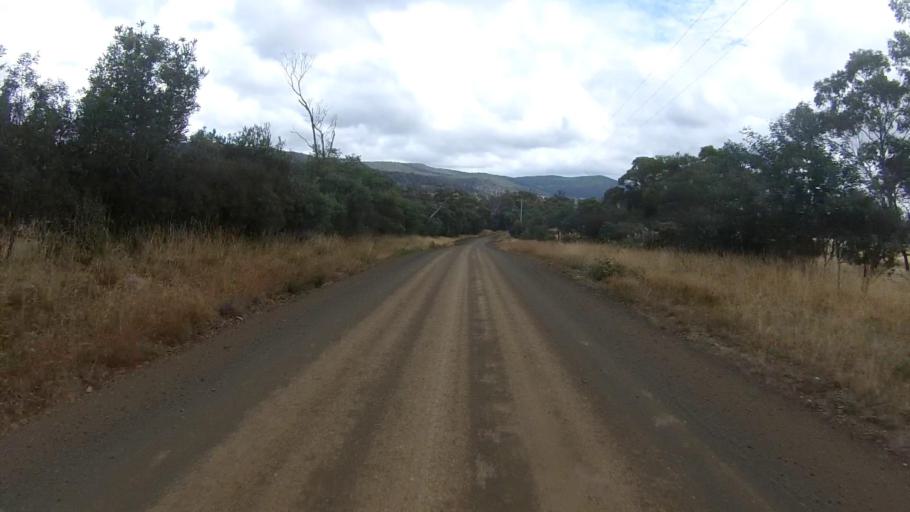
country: AU
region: Tasmania
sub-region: Break O'Day
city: St Helens
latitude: -41.8235
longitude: 147.9865
